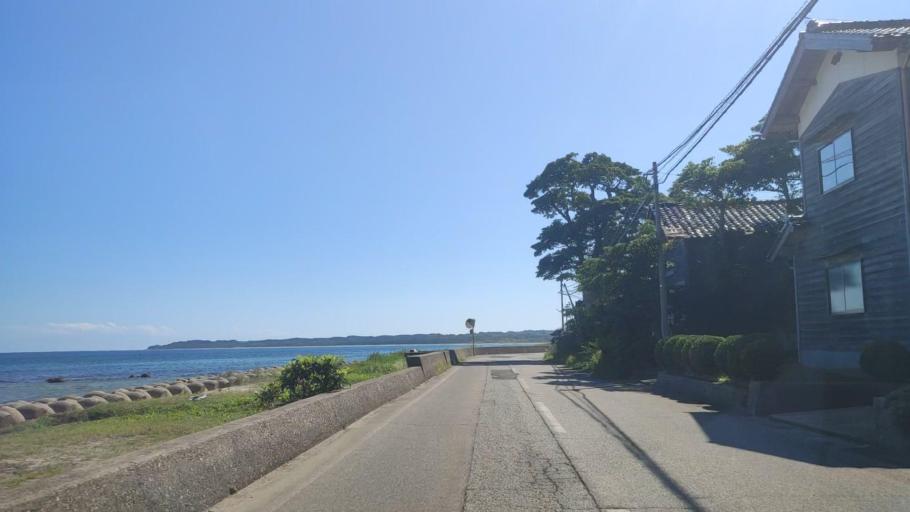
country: JP
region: Toyama
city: Nyuzen
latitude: 37.4927
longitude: 137.3430
